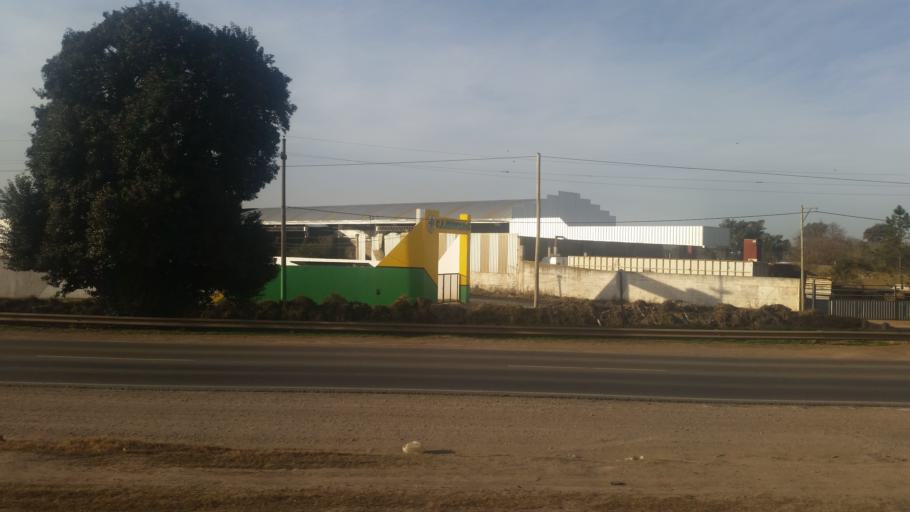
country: AR
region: Cordoba
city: Toledo
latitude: -31.4863
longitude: -64.0809
